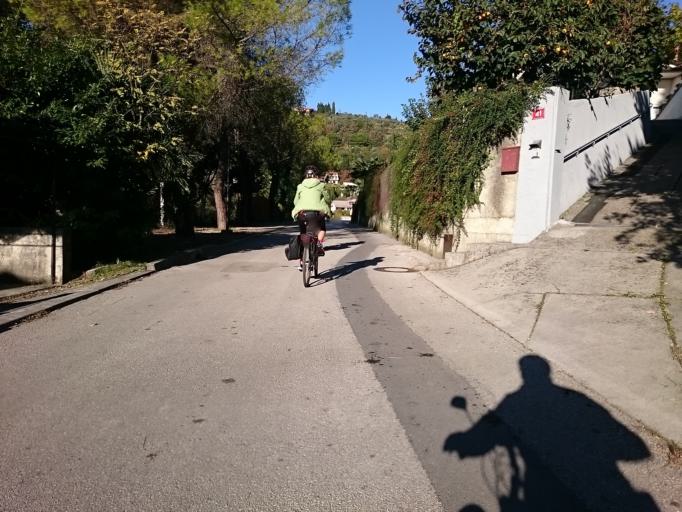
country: SI
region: Piran-Pirano
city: Portoroz
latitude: 45.5143
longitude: 13.5977
